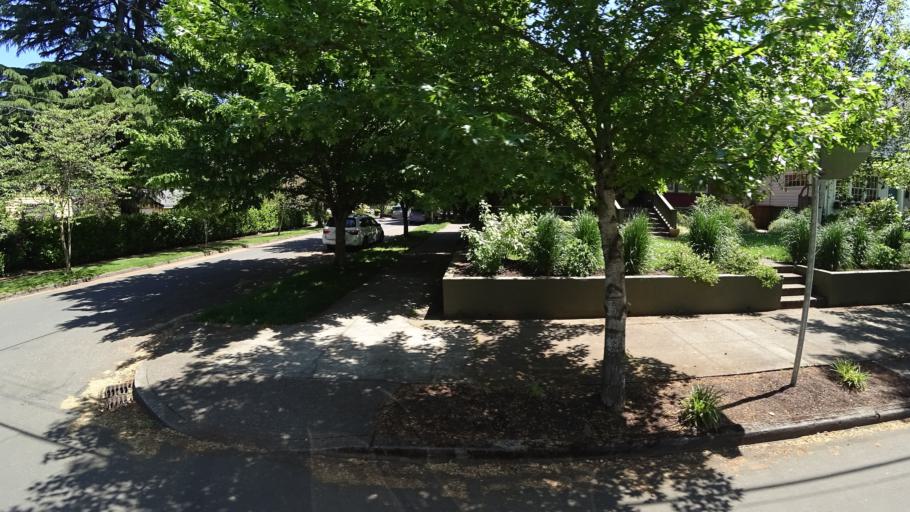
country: US
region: Oregon
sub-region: Multnomah County
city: Portland
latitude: 45.5404
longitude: -122.6382
